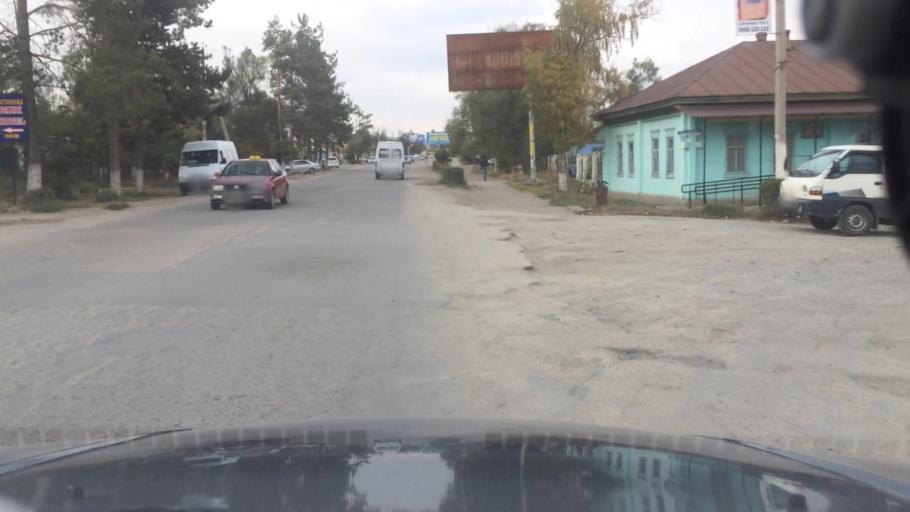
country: KG
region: Ysyk-Koel
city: Karakol
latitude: 42.4890
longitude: 78.3896
